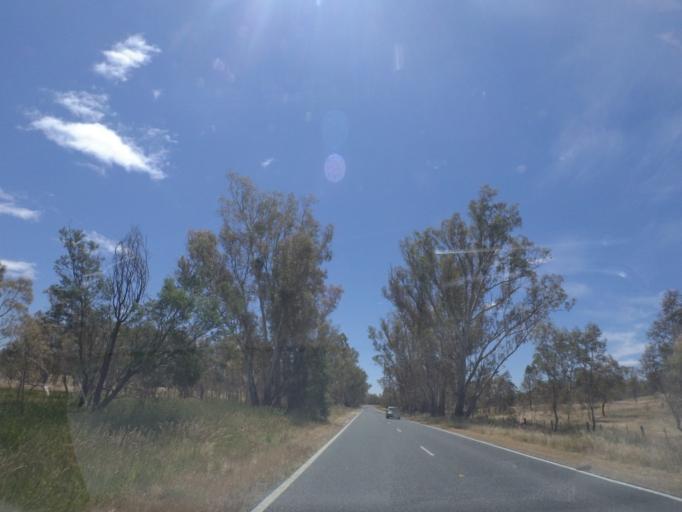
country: AU
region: Victoria
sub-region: Mount Alexander
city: Castlemaine
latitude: -37.1767
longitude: 144.1472
